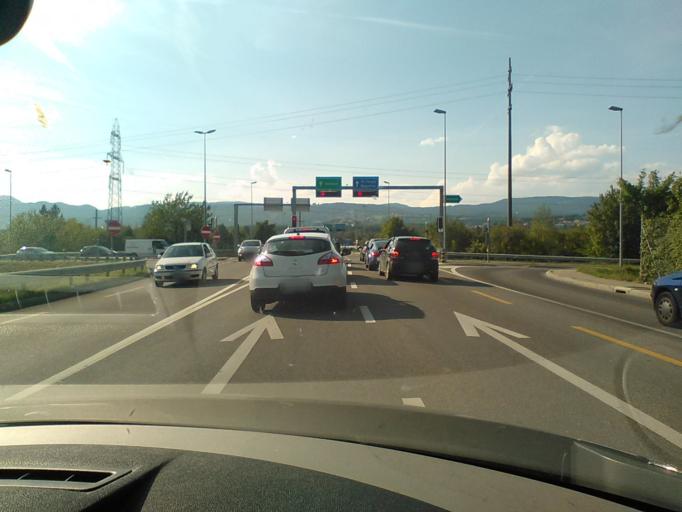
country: CH
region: Vaud
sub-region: Nyon District
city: Gland
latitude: 46.4243
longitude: 6.2581
